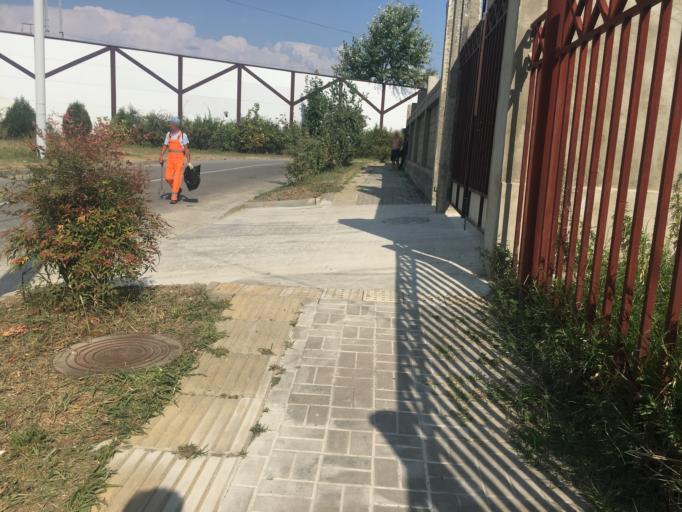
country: RU
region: Krasnodarskiy
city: Vysokoye
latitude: 43.3964
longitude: 39.9988
